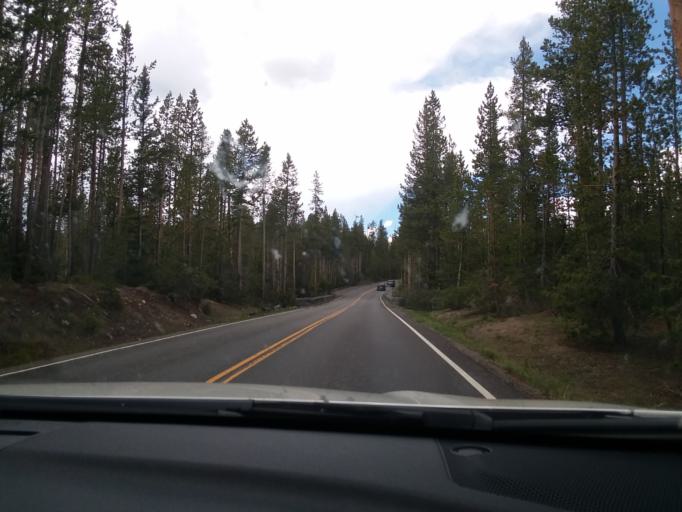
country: US
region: Idaho
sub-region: Teton County
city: Driggs
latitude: 44.1512
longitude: -110.6726
